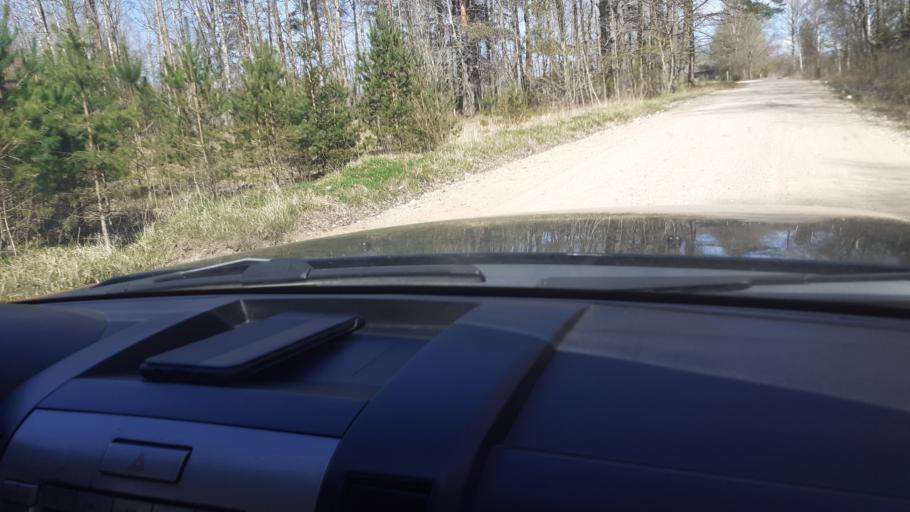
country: LV
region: Kuldigas Rajons
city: Kuldiga
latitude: 56.8472
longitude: 21.9797
